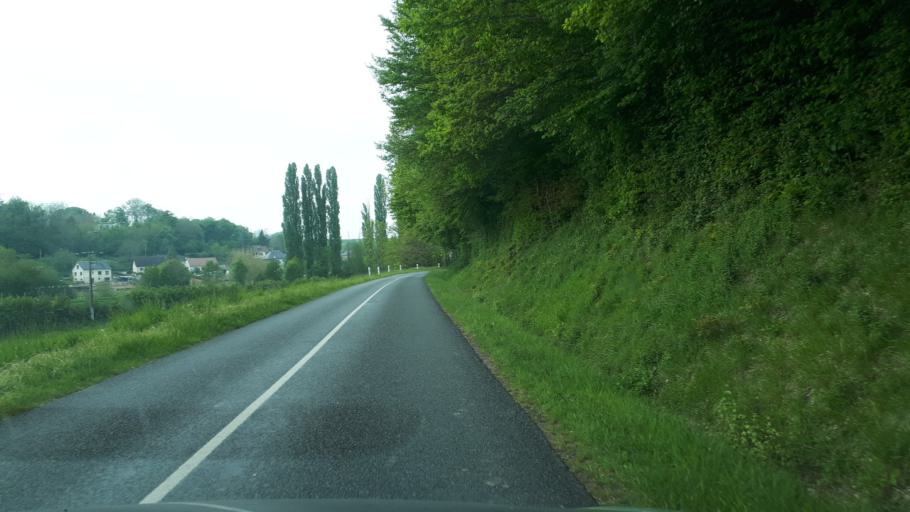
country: FR
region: Centre
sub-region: Departement du Loir-et-Cher
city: Lunay
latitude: 47.8184
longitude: 0.9506
